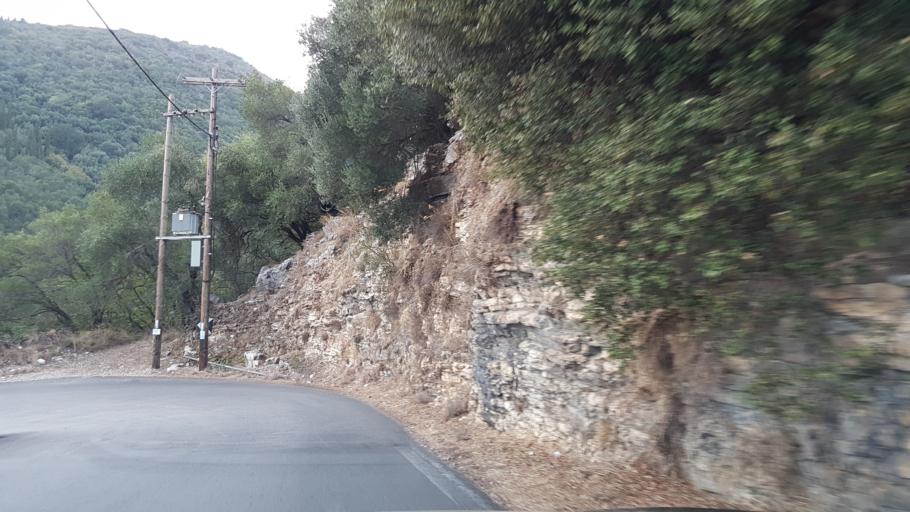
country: GR
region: Ionian Islands
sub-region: Nomos Kerkyras
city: Kontokali
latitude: 39.7349
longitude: 19.9208
